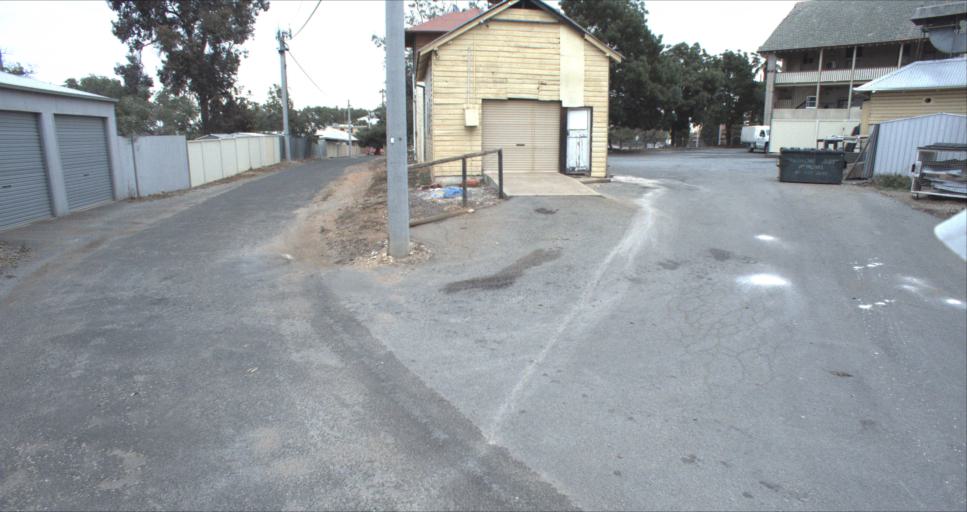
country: AU
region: New South Wales
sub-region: Leeton
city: Leeton
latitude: -34.5512
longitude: 146.4081
